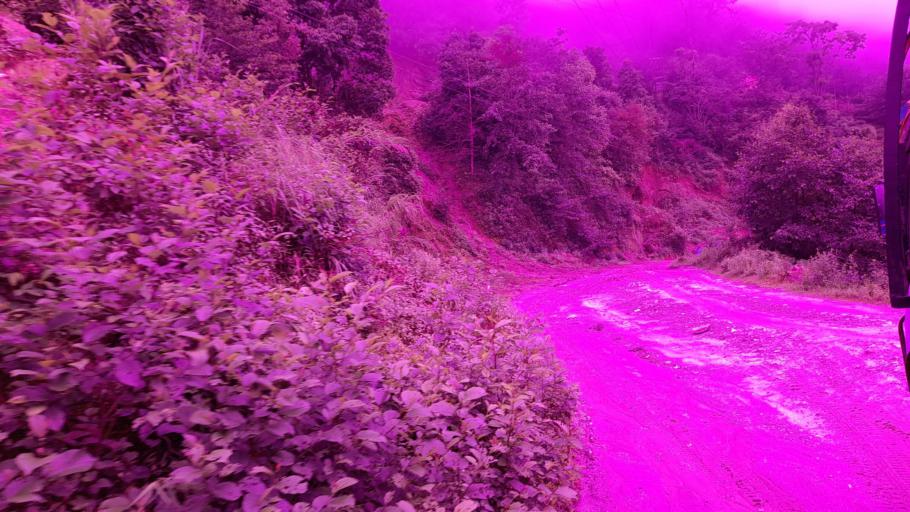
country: NP
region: Central Region
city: Kirtipur
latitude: 27.8126
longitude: 85.2165
